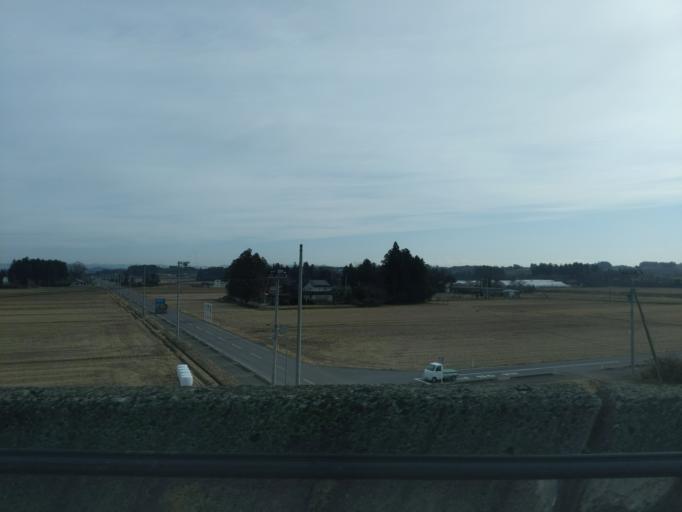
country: JP
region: Iwate
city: Ichinoseki
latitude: 38.7556
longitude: 141.0755
